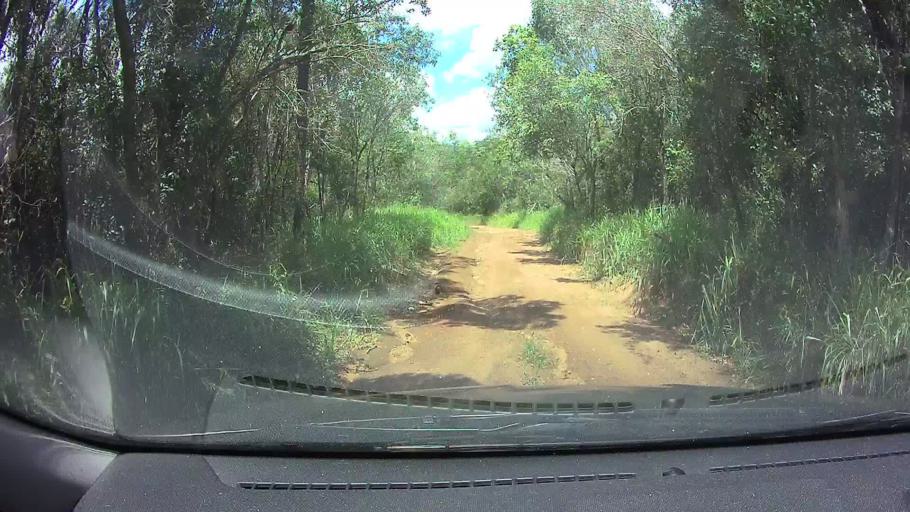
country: PY
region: Paraguari
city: La Colmena
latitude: -25.9720
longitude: -56.7298
